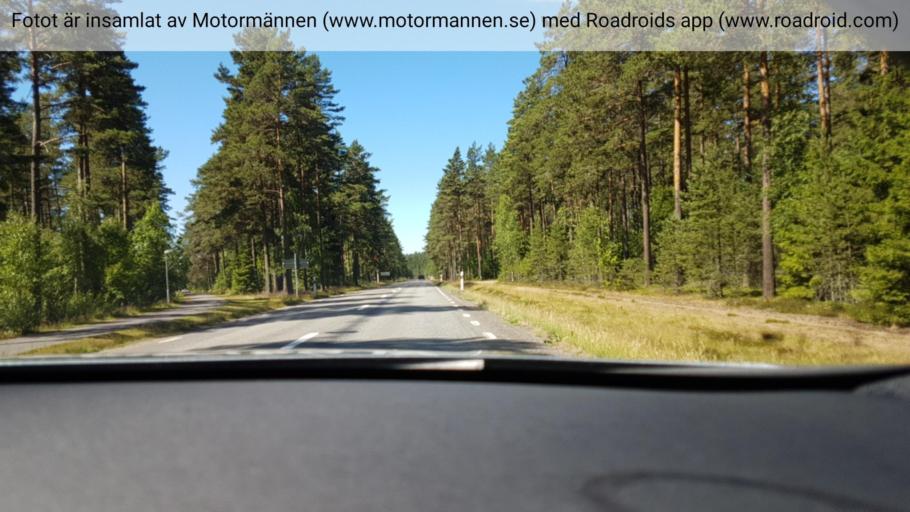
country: SE
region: Joenkoeping
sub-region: Mullsjo Kommun
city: Mullsjoe
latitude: 57.9031
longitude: 13.8563
